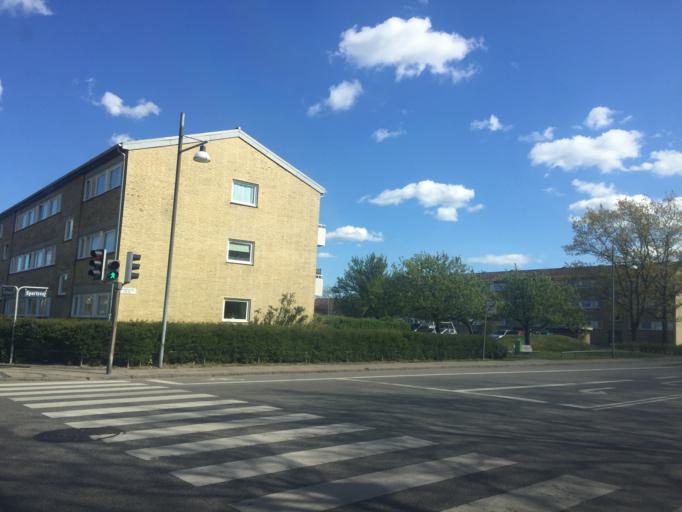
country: DK
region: Capital Region
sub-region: Albertslund Kommune
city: Albertslund
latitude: 55.6672
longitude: 12.3790
